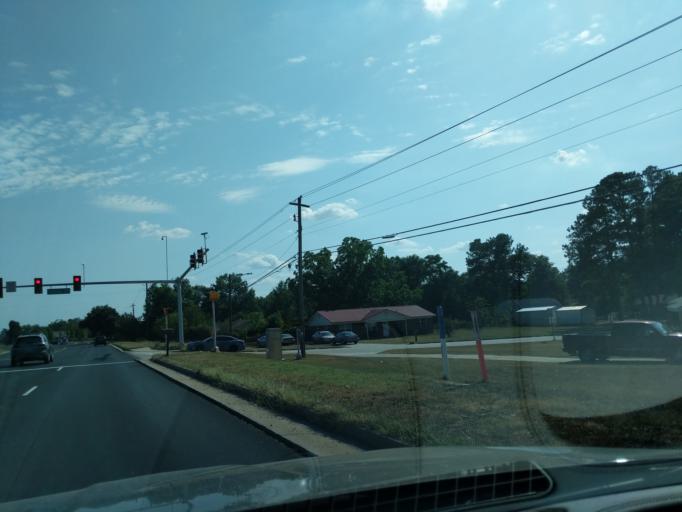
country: US
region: Georgia
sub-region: Columbia County
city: Evans
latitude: 33.4935
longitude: -82.1373
